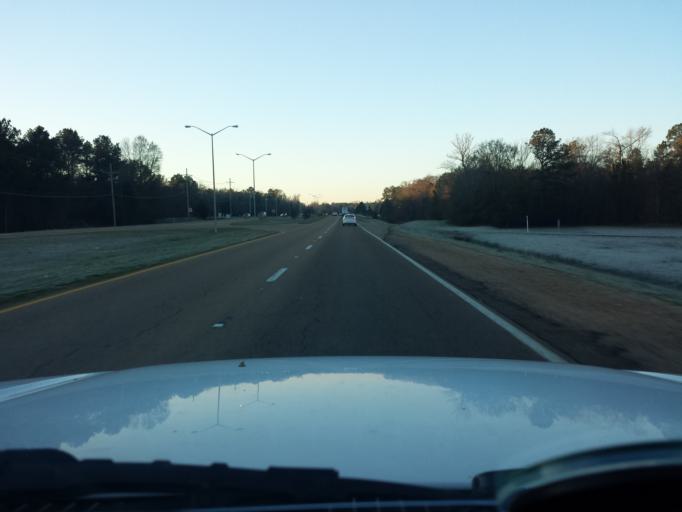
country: US
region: Mississippi
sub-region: Rankin County
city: Flowood
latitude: 32.2989
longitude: -90.1431
